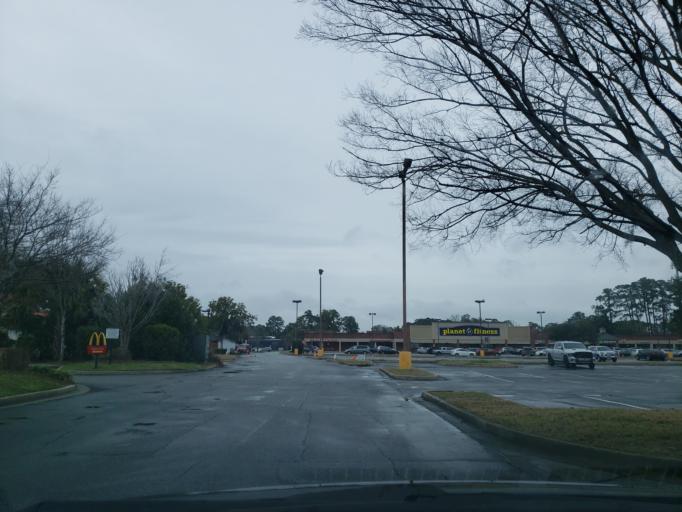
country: US
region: Georgia
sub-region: Chatham County
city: Isle of Hope
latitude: 32.0068
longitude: -81.1000
